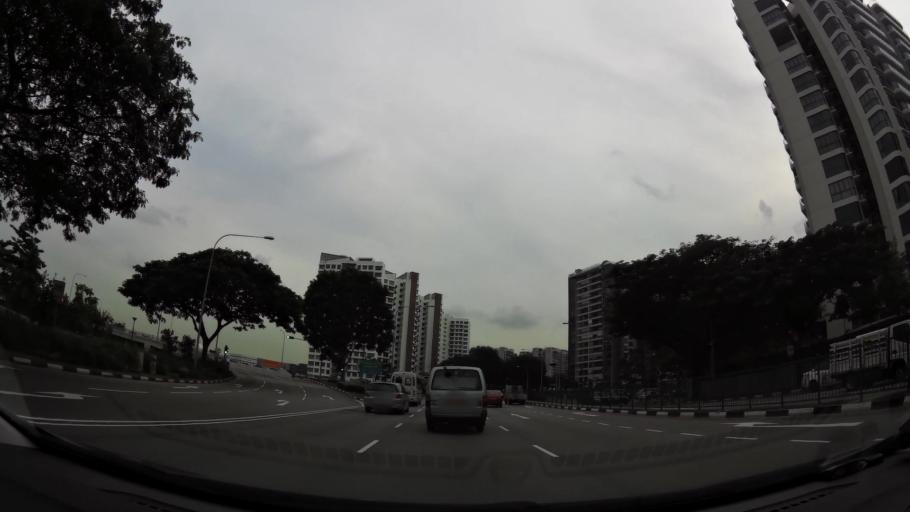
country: MY
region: Johor
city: Kampung Pasir Gudang Baru
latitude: 1.3811
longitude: 103.9035
